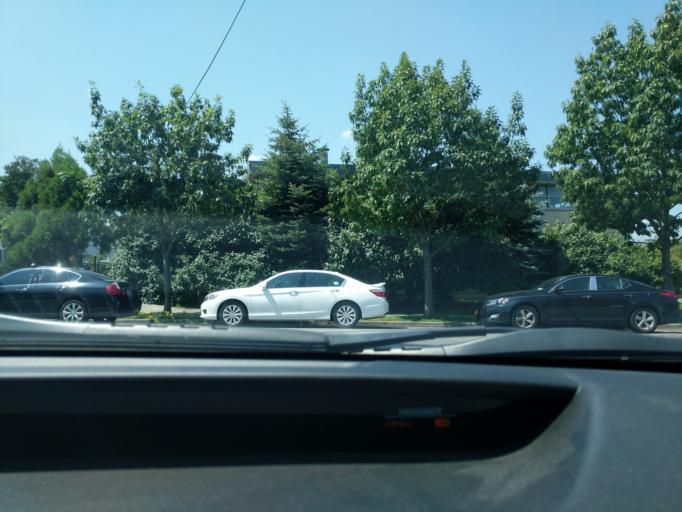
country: US
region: New Jersey
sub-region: Middlesex County
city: Carteret
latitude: 40.5540
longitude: -74.2127
